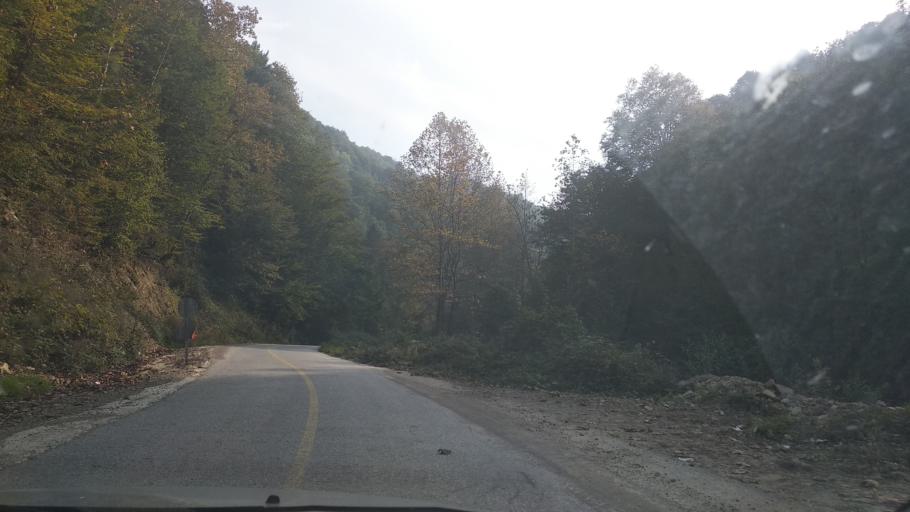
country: TR
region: Duzce
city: Kaynasli
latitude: 40.7124
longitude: 31.2661
